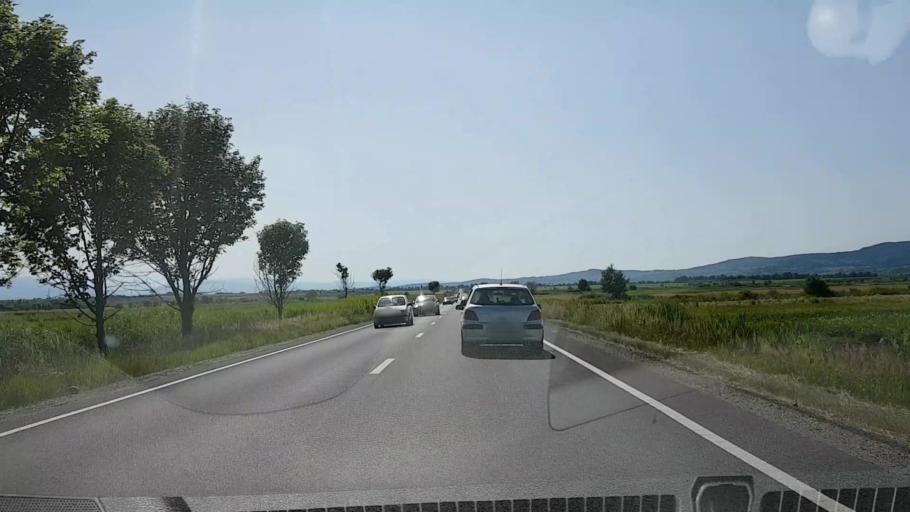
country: RO
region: Sibiu
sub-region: Comuna Porumbacu de Jos
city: Porumbacu de Jos
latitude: 45.7569
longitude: 24.4942
